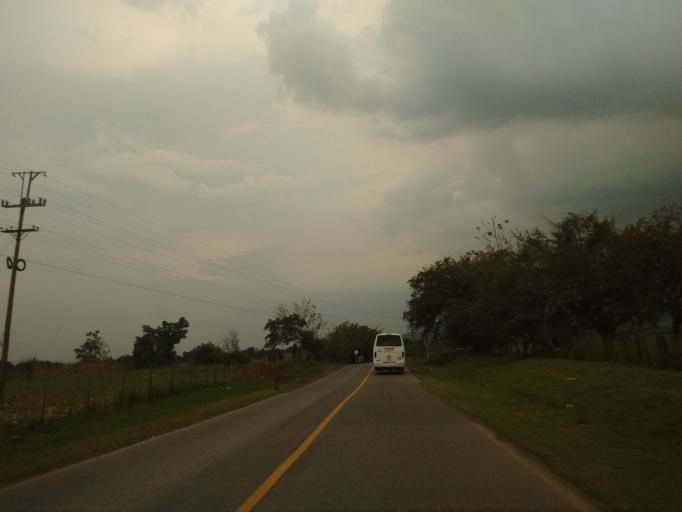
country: CO
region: Cauca
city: Caloto
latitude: 3.0566
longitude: -76.3746
